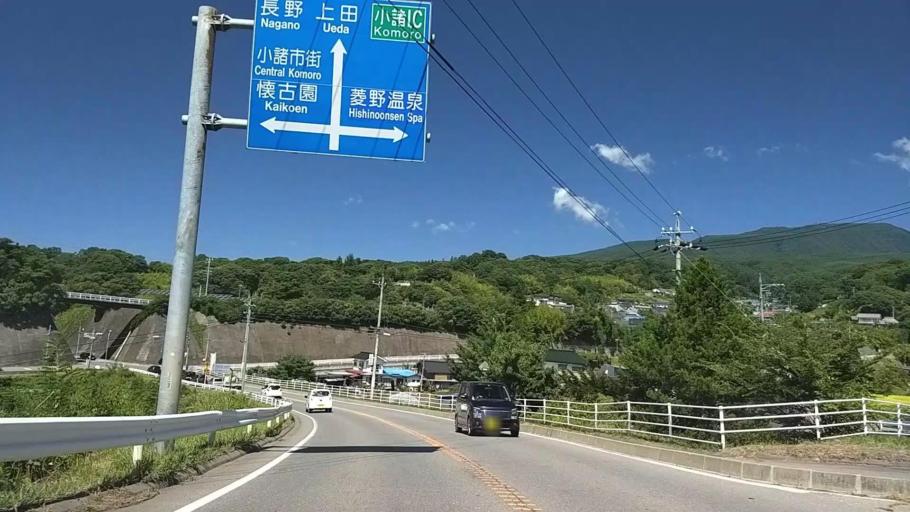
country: JP
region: Nagano
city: Komoro
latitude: 36.3484
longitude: 138.4323
